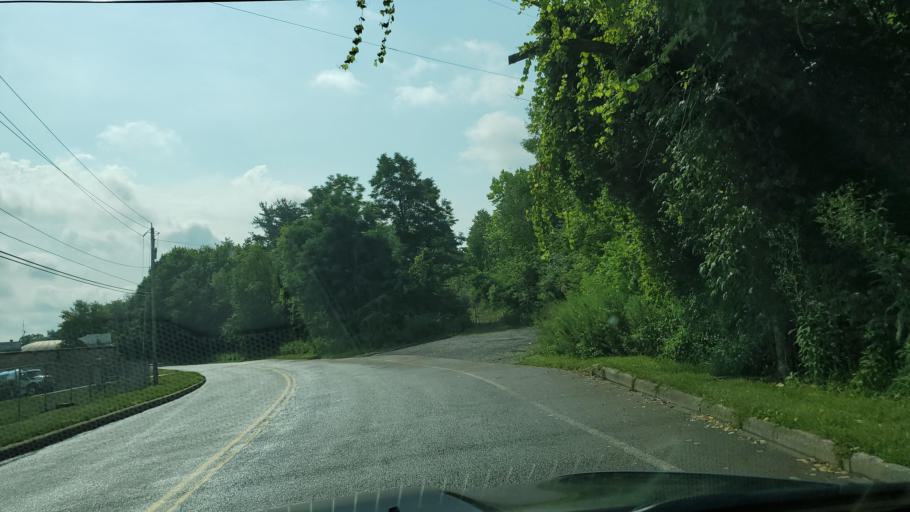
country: US
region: Ohio
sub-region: Mahoning County
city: Struthers
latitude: 41.0478
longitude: -80.5729
